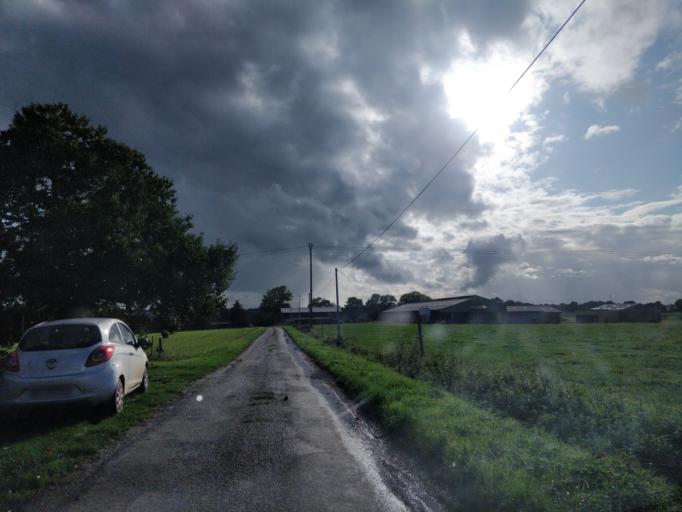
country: FR
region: Brittany
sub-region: Departement d'Ille-et-Vilaine
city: Chateaubourg
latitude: 48.1221
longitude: -1.4268
